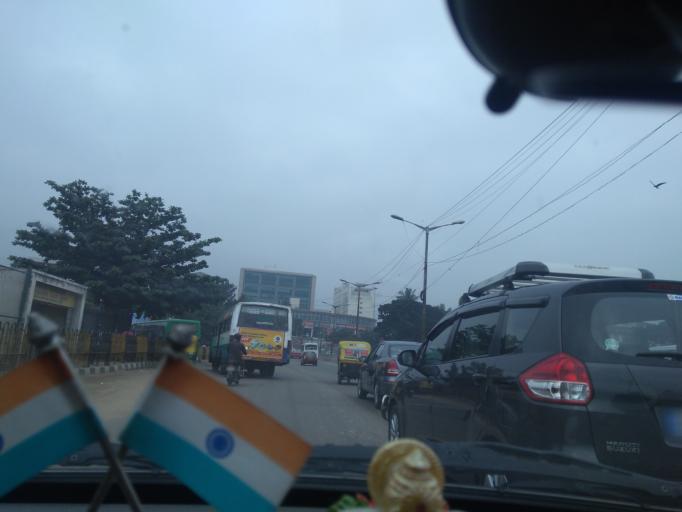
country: IN
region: Karnataka
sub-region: Bangalore Urban
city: Bangalore
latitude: 12.9825
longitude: 77.5627
